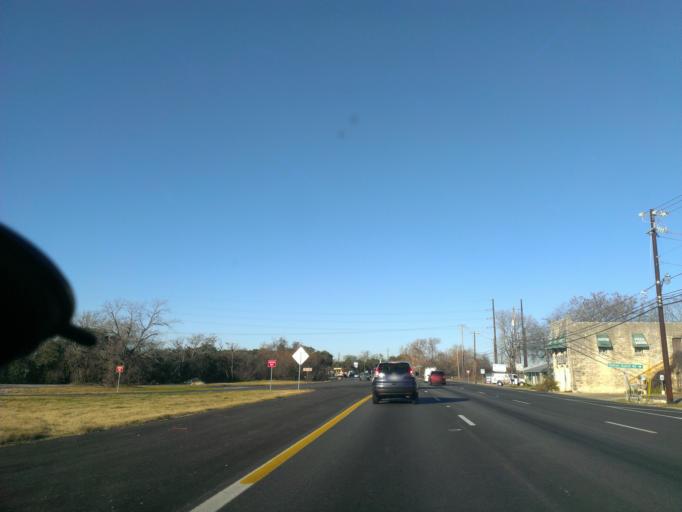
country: US
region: Texas
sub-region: Travis County
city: Barton Creek
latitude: 30.2355
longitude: -97.8581
